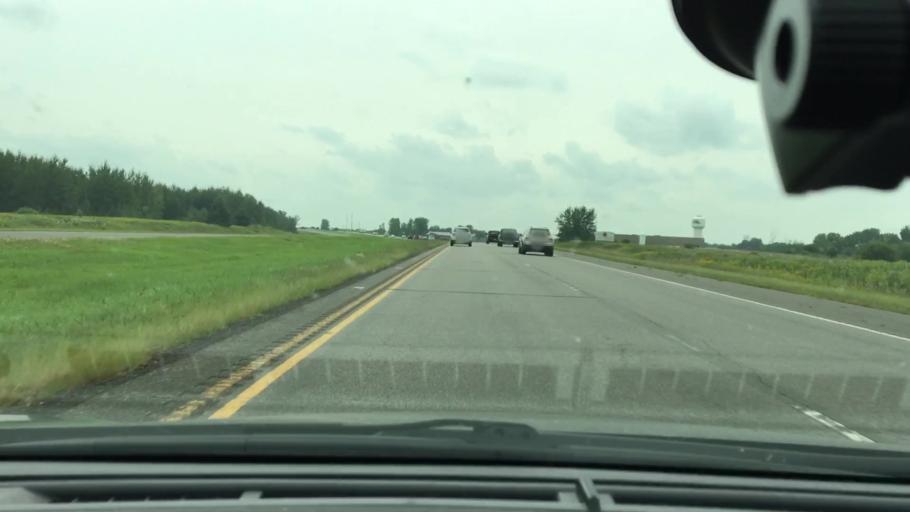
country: US
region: Minnesota
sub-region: Mille Lacs County
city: Milaca
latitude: 45.7713
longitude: -93.6459
